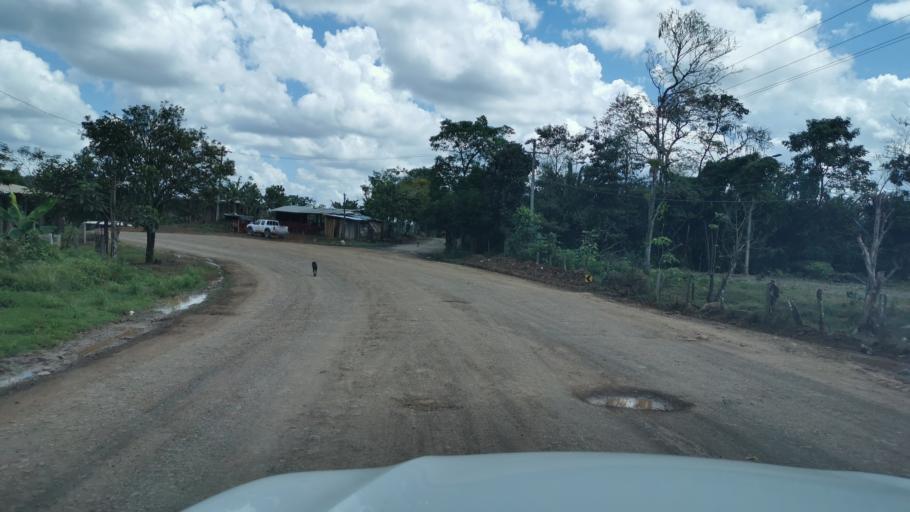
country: NI
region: Atlantico Sur
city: Rama
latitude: 12.2286
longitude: -84.2327
